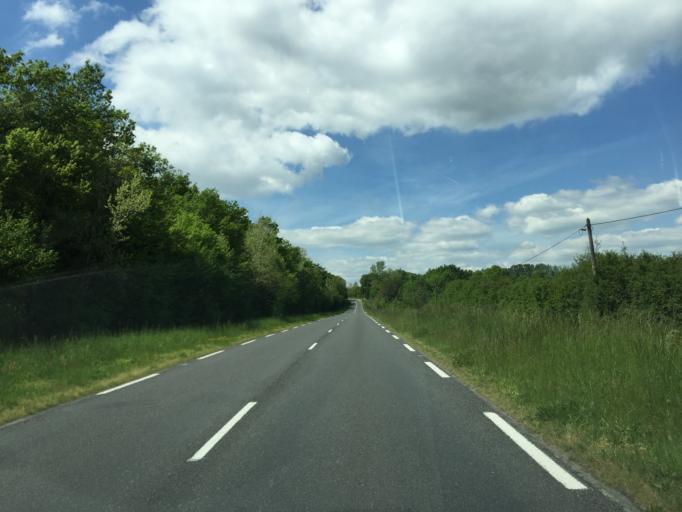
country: FR
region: Auvergne
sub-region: Departement de l'Allier
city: Brugheas
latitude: 46.0717
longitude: 3.3131
